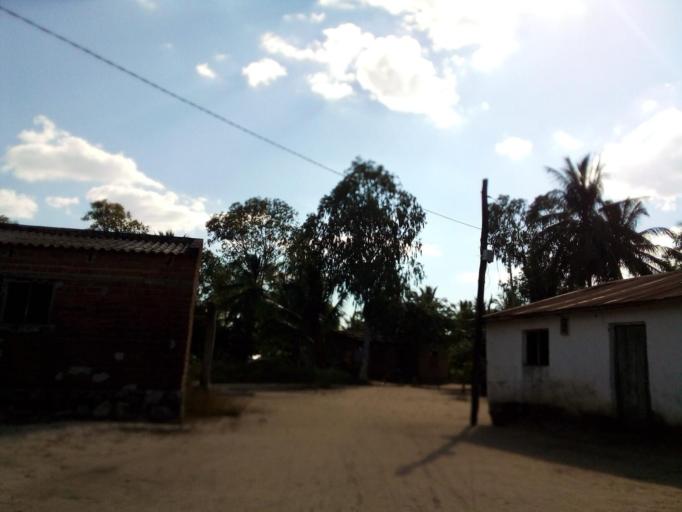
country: MZ
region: Zambezia
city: Quelimane
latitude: -17.5777
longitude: 36.7045
